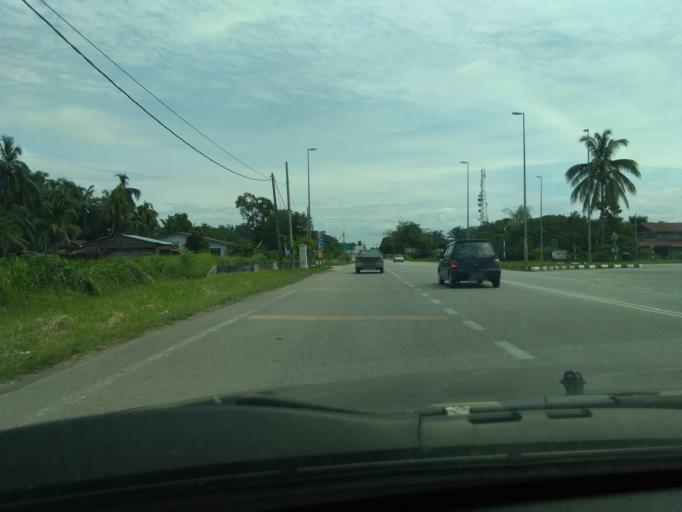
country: MY
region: Perak
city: Bagan Serai
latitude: 5.0601
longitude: 100.5943
